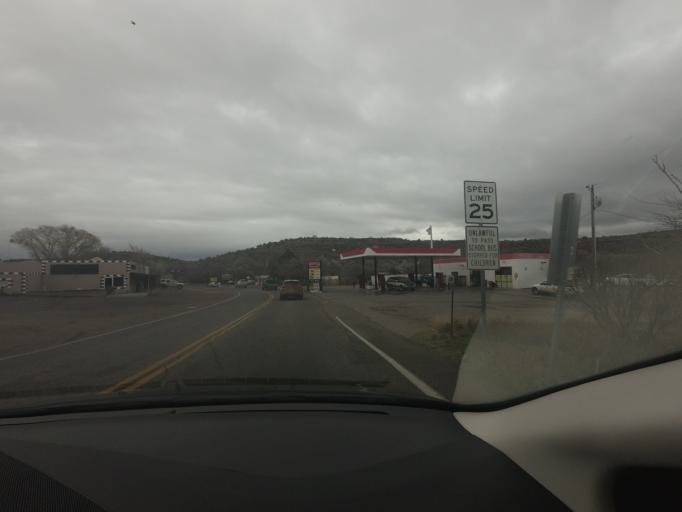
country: US
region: Arizona
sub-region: Yavapai County
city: Lake Montezuma
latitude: 34.6378
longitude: -111.8152
